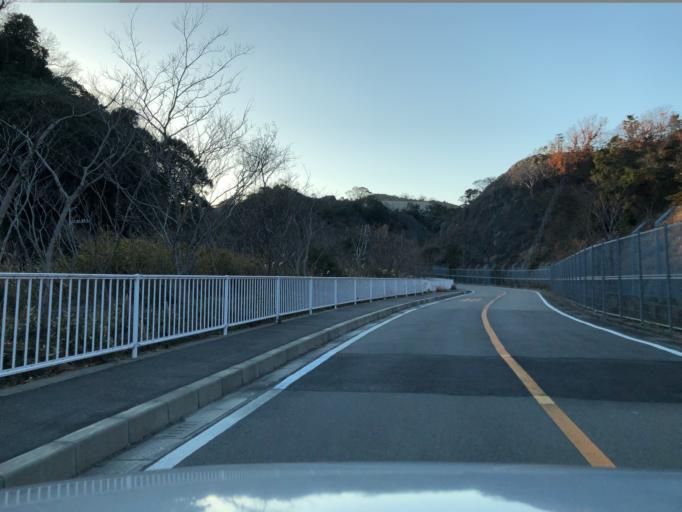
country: JP
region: Wakayama
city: Tanabe
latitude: 33.6628
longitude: 135.3713
